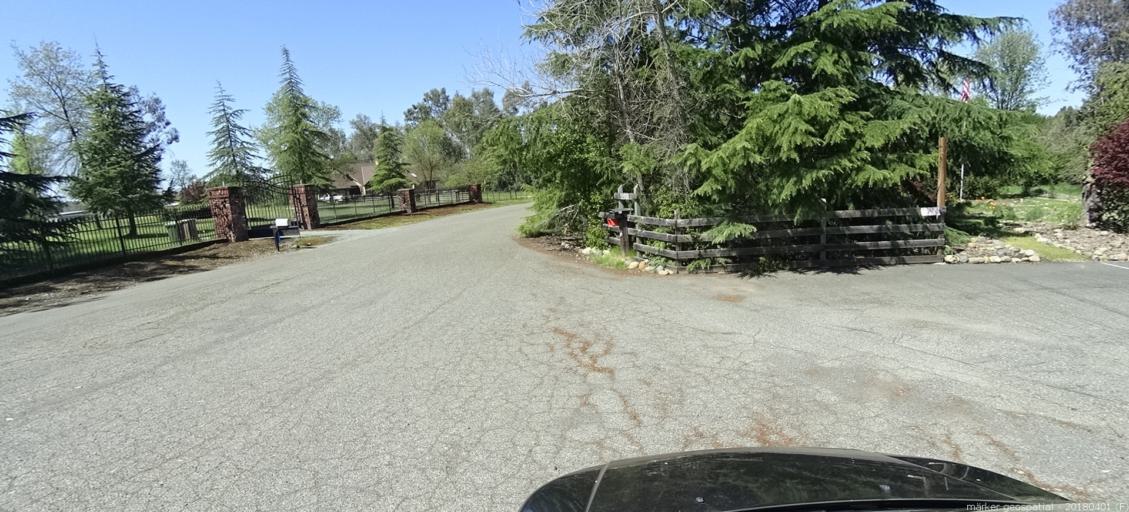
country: US
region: California
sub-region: Sacramento County
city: Wilton
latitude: 38.4137
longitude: -121.2305
